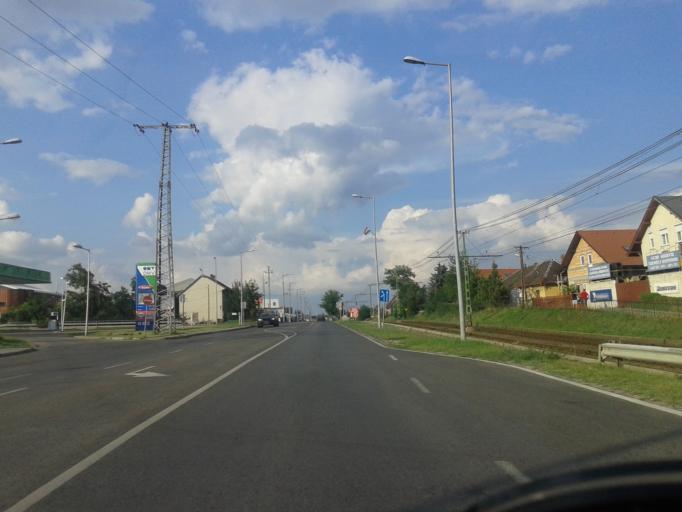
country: HU
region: Budapest
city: Budapest XXIII. keruelet
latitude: 47.3863
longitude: 19.1103
